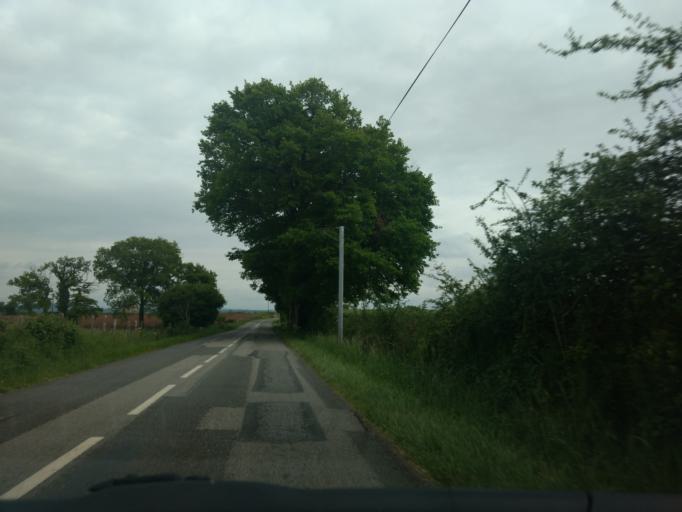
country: FR
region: Midi-Pyrenees
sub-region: Departement de l'Aveyron
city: Montbazens
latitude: 44.5054
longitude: 2.1946
